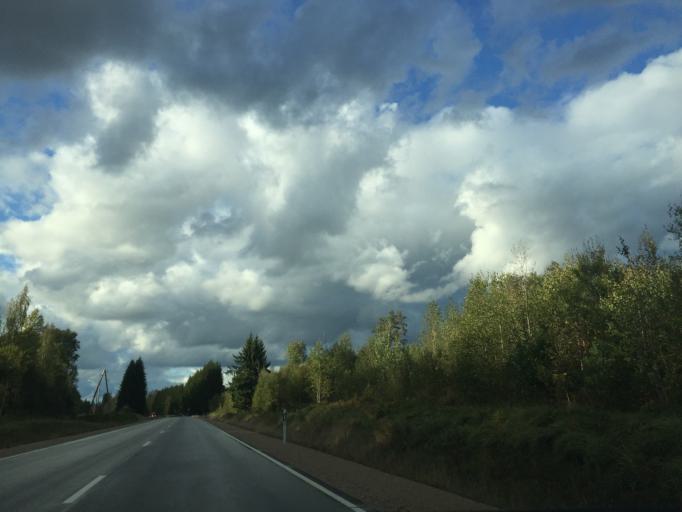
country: LV
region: Ligatne
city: Ligatne
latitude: 57.1503
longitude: 25.0731
